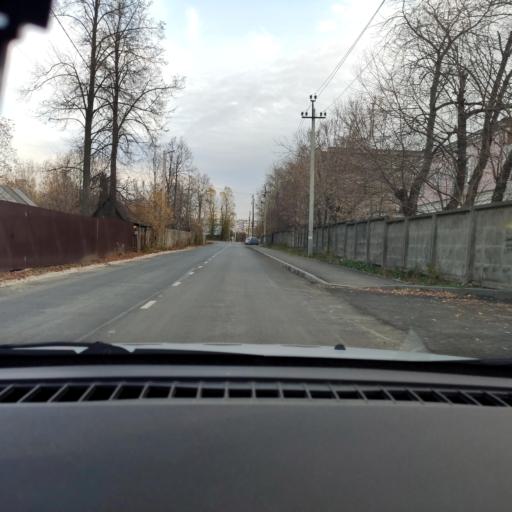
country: RU
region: Perm
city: Kondratovo
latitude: 57.9627
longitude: 56.1540
